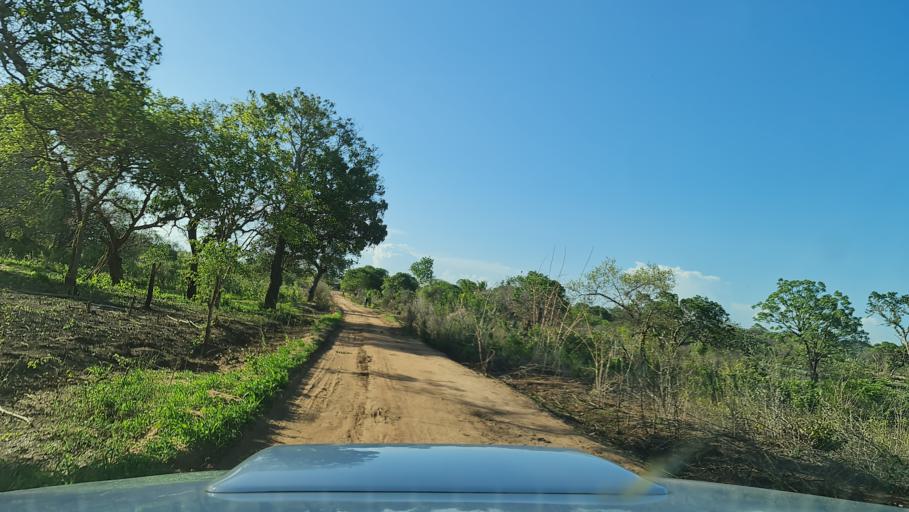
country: MZ
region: Nampula
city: Nacala
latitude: -14.7016
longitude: 40.3291
